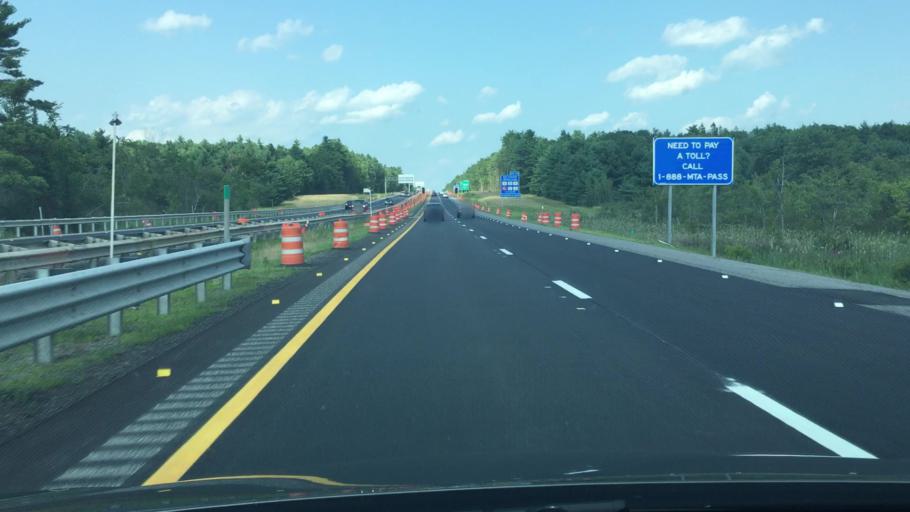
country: US
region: Maine
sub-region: Kennebec County
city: Gardiner
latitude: 44.1925
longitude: -69.8477
